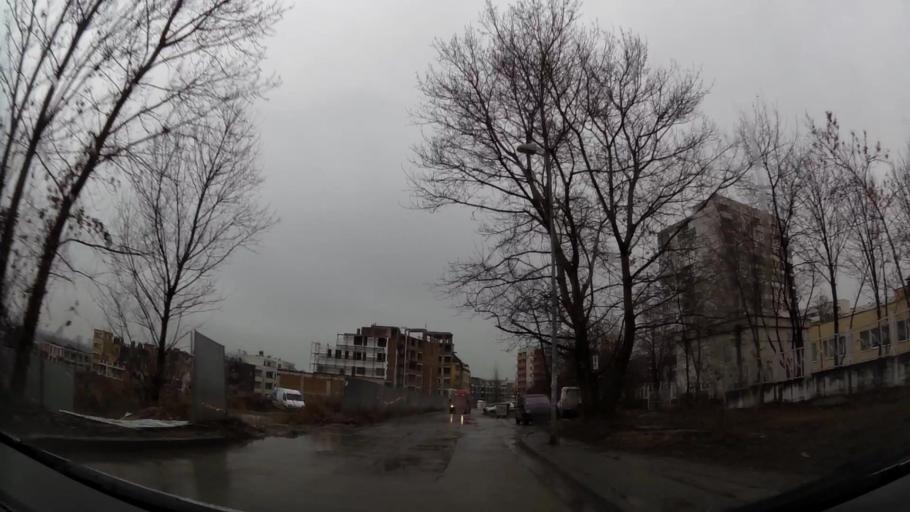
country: BG
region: Sofia-Capital
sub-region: Stolichna Obshtina
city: Sofia
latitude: 42.6526
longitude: 23.3390
